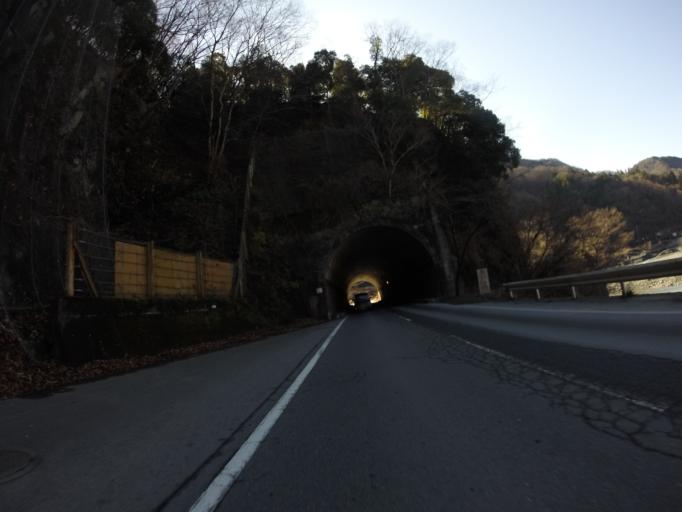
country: JP
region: Yamanashi
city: Ryuo
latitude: 35.4236
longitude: 138.4055
